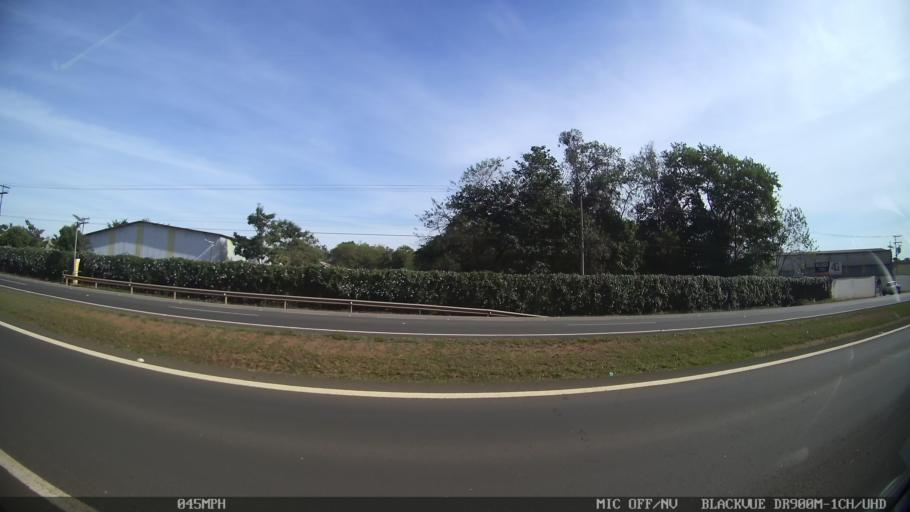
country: BR
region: Sao Paulo
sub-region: Piracicaba
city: Piracicaba
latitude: -22.7741
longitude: -47.6493
